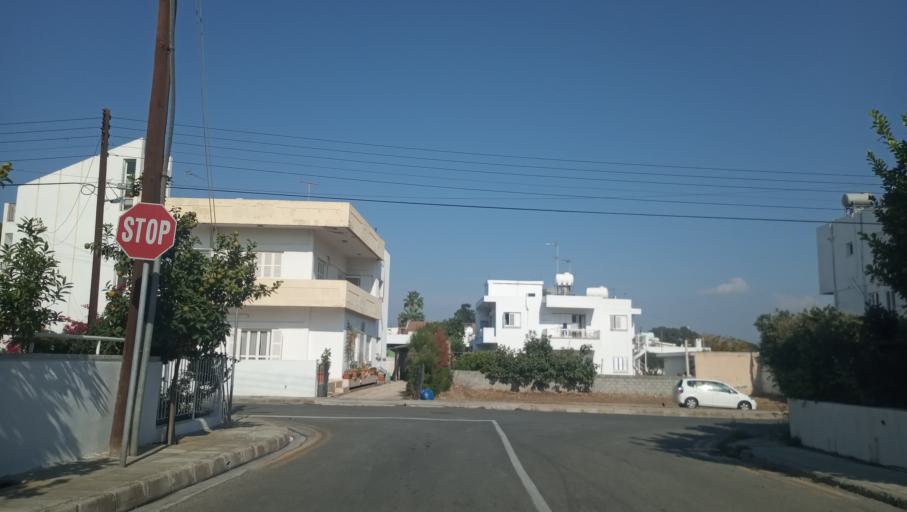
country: CY
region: Lefkosia
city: Nicosia
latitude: 35.1418
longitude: 33.3774
